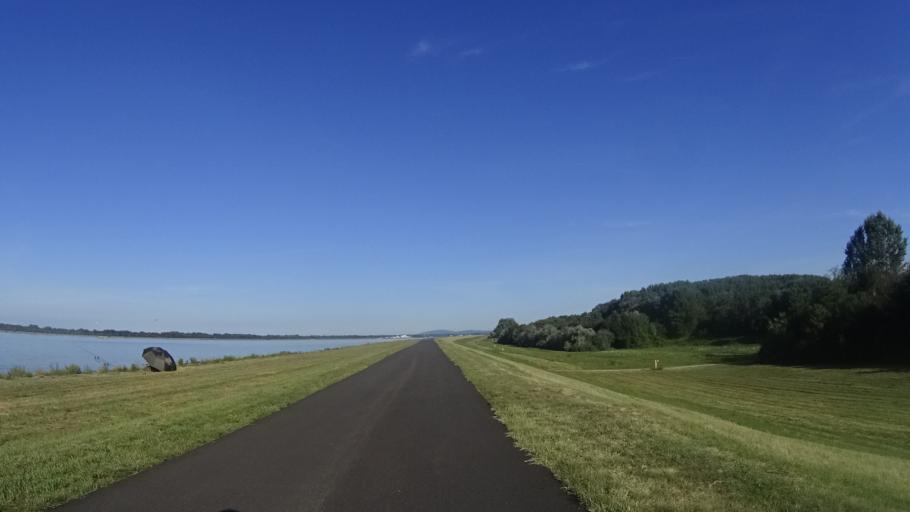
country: SK
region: Trnavsky
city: Samorin
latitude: 48.0250
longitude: 17.2689
